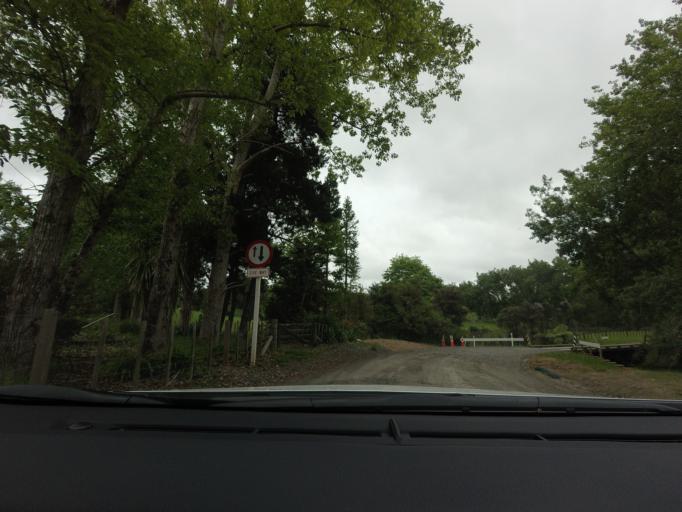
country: NZ
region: Auckland
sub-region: Auckland
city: Warkworth
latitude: -36.5013
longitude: 174.6236
